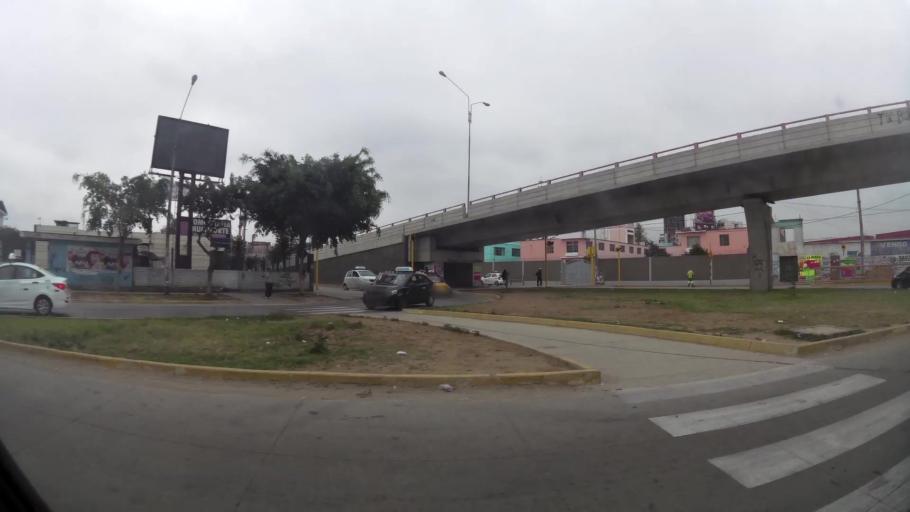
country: PE
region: La Libertad
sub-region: Provincia de Trujillo
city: Trujillo
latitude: -8.1051
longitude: -79.0357
